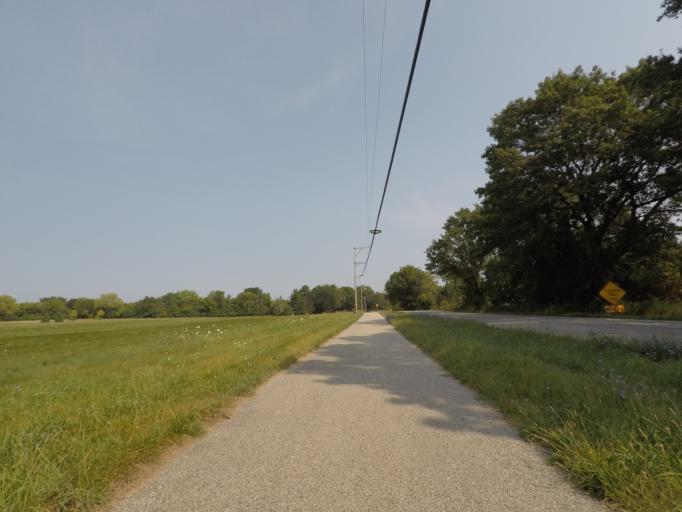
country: US
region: Wisconsin
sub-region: Waukesha County
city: Delafield
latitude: 43.0308
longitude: -88.4143
